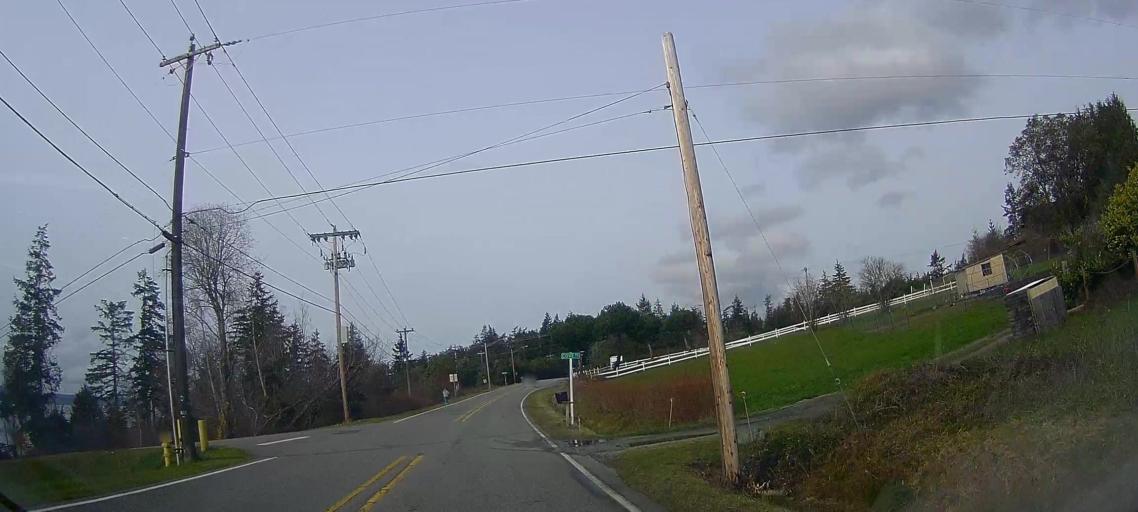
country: US
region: Washington
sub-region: Island County
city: Camano
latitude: 48.1555
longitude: -122.5157
